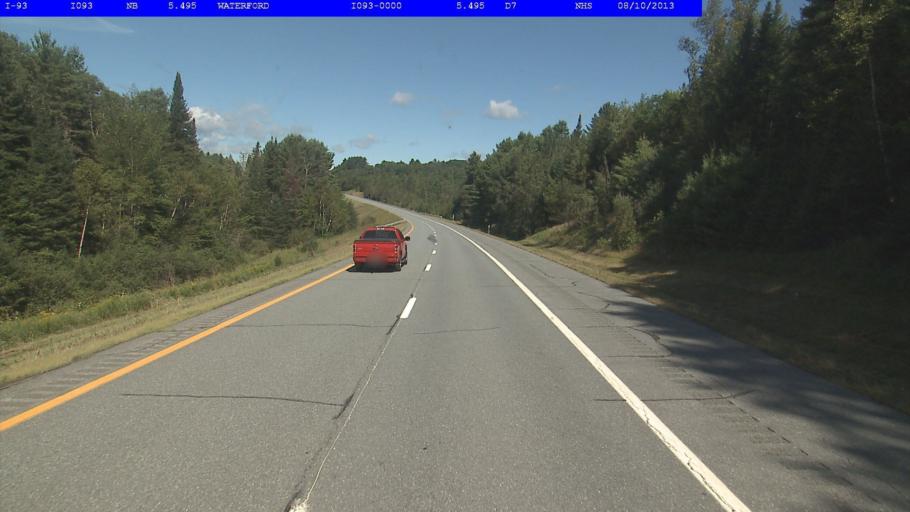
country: US
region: Vermont
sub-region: Caledonia County
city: Saint Johnsbury
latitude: 44.4141
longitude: -71.9228
